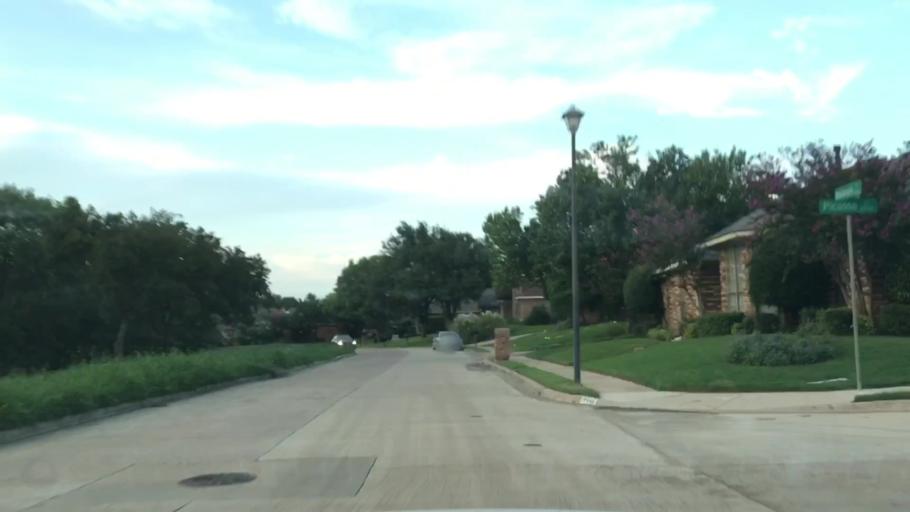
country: US
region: Texas
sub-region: Dallas County
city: Addison
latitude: 33.0042
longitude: -96.8651
